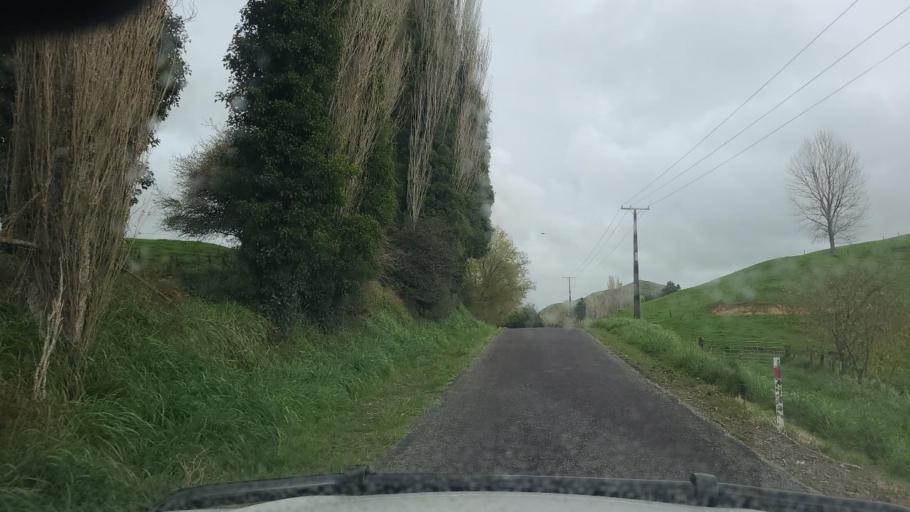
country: NZ
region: Taranaki
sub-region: South Taranaki District
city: Eltham
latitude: -39.2674
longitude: 174.4150
